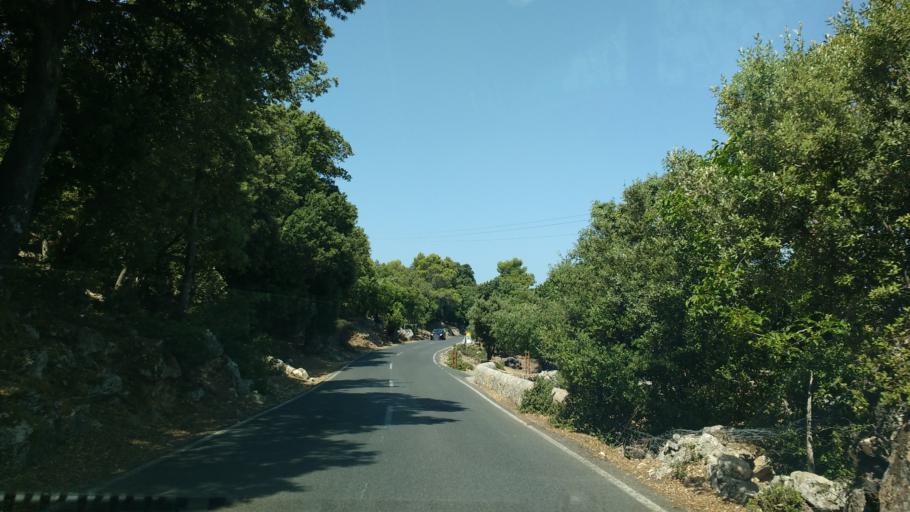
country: ES
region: Balearic Islands
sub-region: Illes Balears
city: Escorca
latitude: 39.8249
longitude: 2.8500
